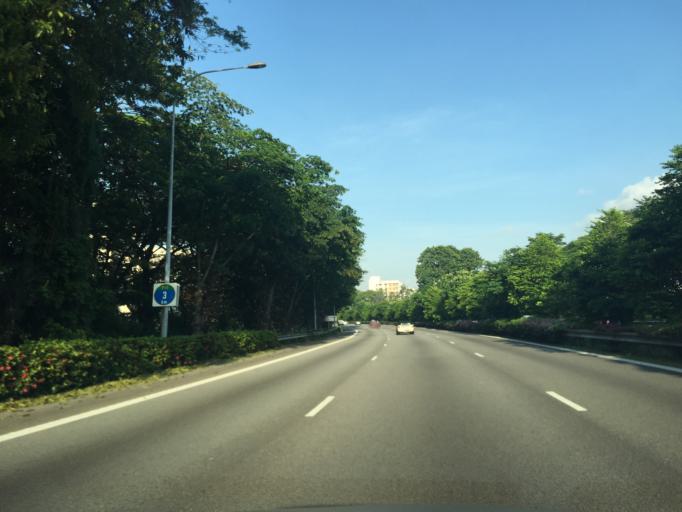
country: SG
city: Singapore
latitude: 1.3505
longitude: 103.9594
